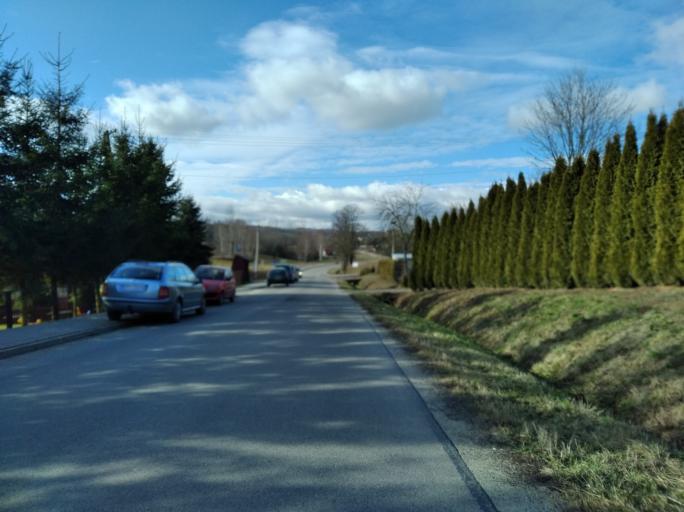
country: PL
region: Subcarpathian Voivodeship
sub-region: Powiat strzyzowski
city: Wisniowa
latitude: 49.9122
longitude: 21.6804
